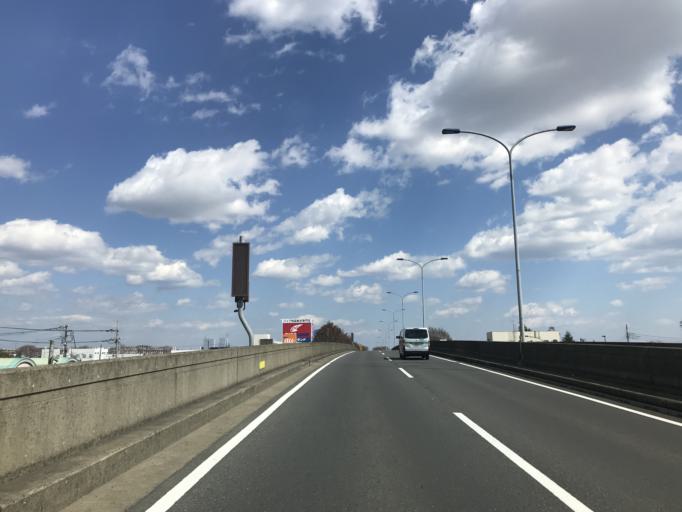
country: JP
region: Ibaraki
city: Mito-shi
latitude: 36.3477
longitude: 140.4631
